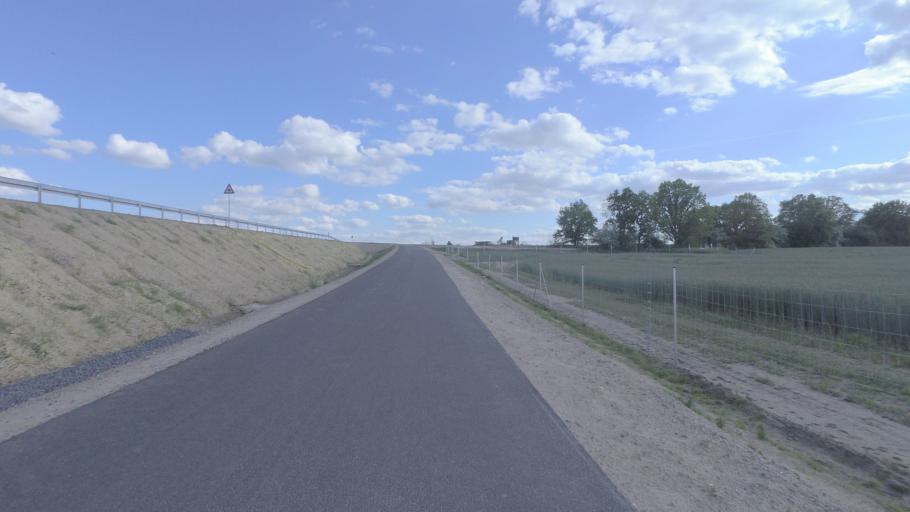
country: DE
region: Brandenburg
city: Stahnsdorf
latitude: 52.3724
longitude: 13.2372
